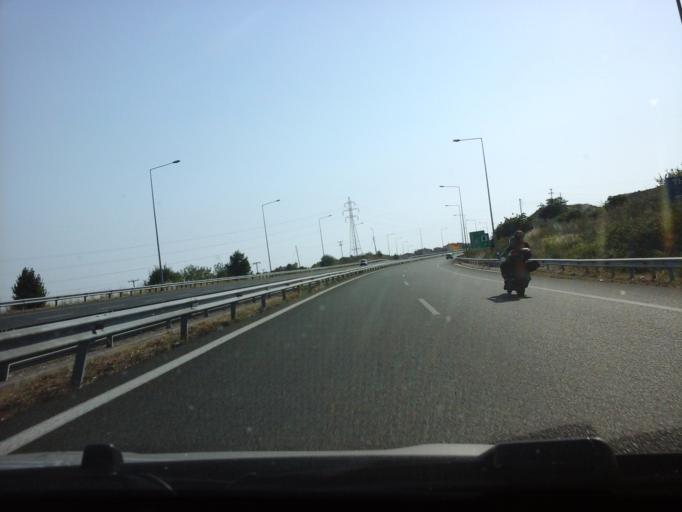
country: GR
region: East Macedonia and Thrace
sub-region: Nomos Evrou
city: Alexandroupoli
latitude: 40.8612
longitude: 25.7577
